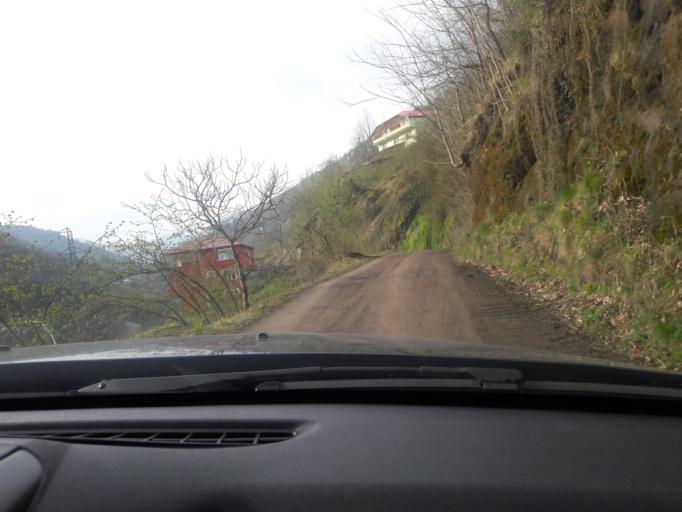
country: TR
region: Trabzon
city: Salpazari
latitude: 40.9707
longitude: 39.1967
